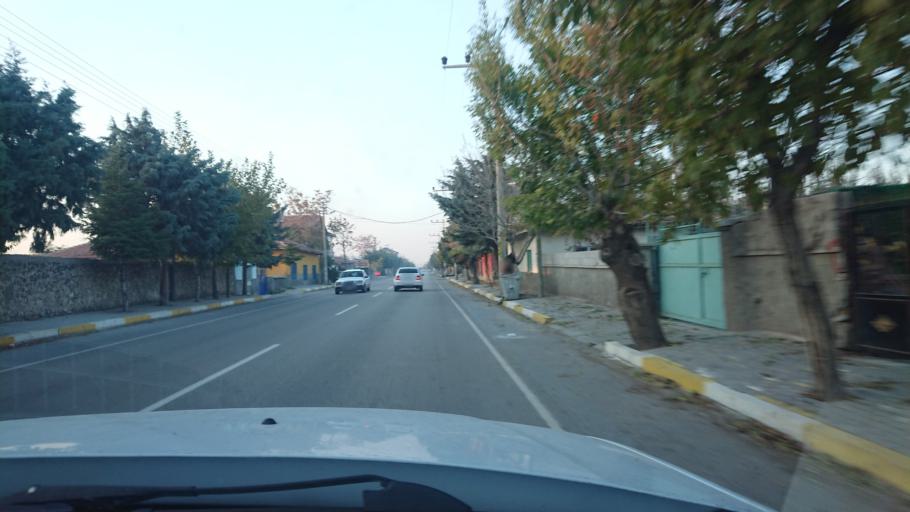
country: TR
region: Aksaray
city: Aksaray
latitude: 38.3027
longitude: 34.0700
